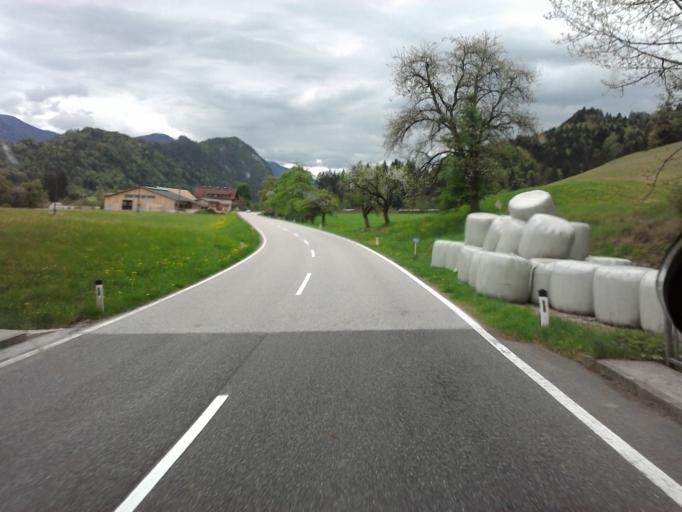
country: AT
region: Upper Austria
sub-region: Politischer Bezirk Kirchdorf an der Krems
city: Rossleithen
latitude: 47.7436
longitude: 14.2535
